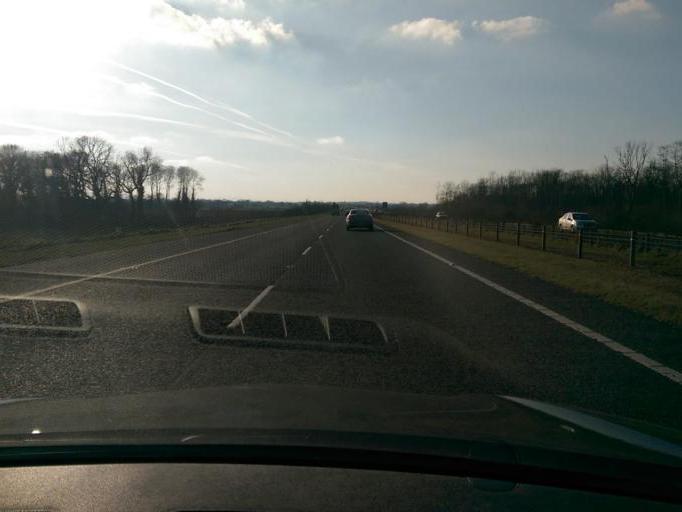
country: IE
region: Leinster
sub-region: Kildare
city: Monasterevin
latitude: 53.1136
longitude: -7.0686
